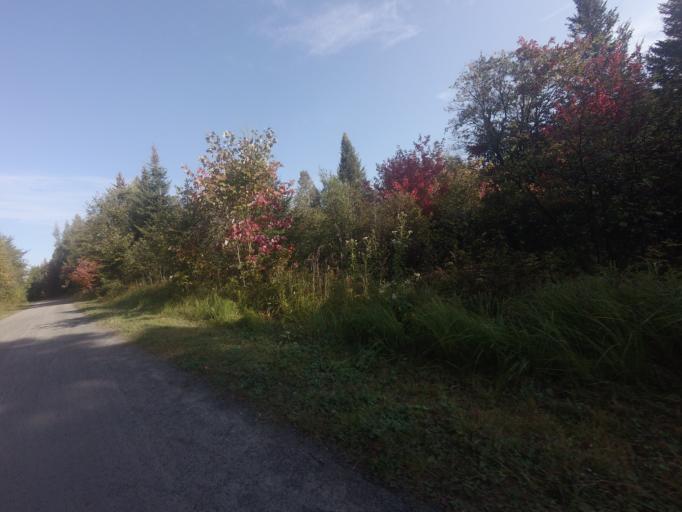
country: CA
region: Quebec
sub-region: Laurentides
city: Val-David
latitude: 46.0203
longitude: -74.1908
